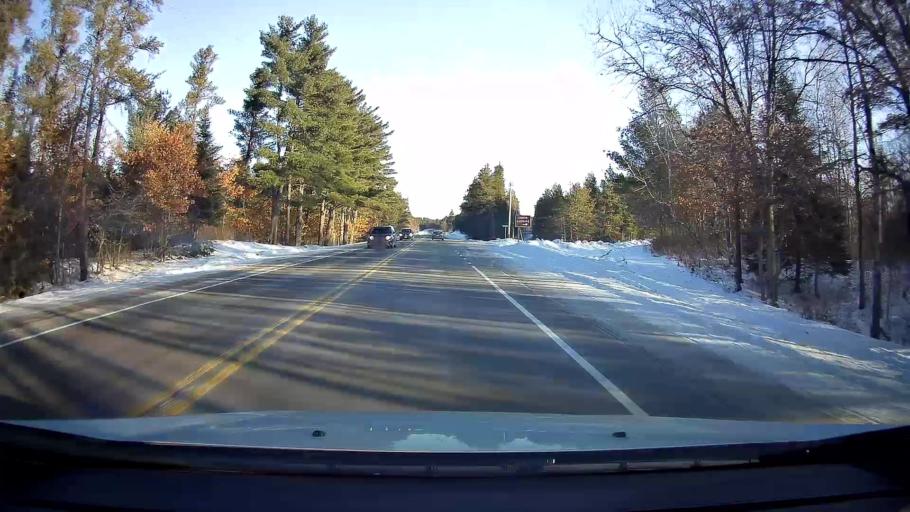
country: US
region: Wisconsin
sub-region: Sawyer County
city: Hayward
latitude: 45.9532
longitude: -91.6836
